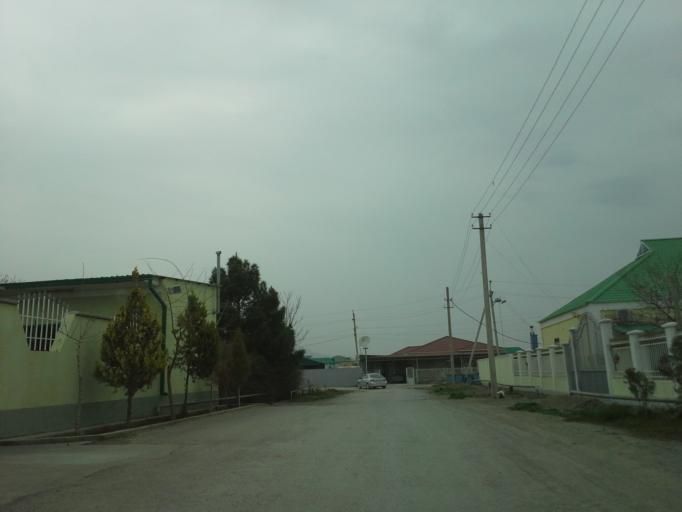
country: TM
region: Ahal
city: Abadan
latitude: 37.9755
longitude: 58.2264
